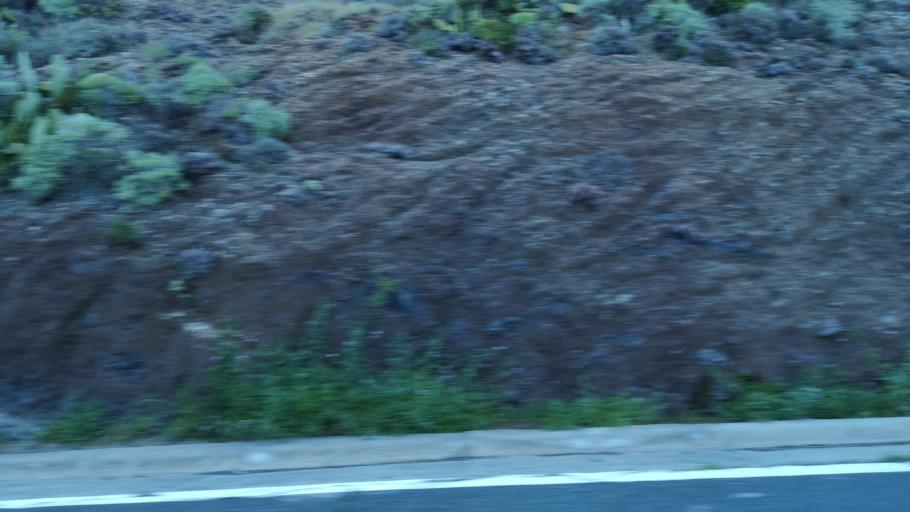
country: ES
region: Canary Islands
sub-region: Provincia de Santa Cruz de Tenerife
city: Alajero
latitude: 28.0798
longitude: -17.2438
